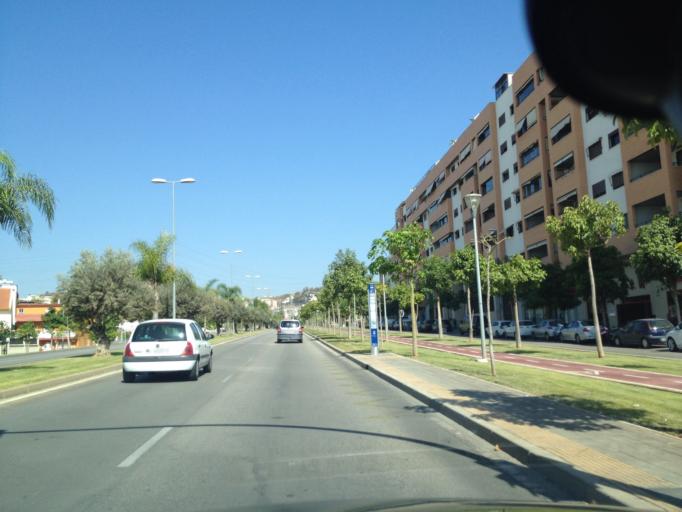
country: ES
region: Andalusia
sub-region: Provincia de Malaga
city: Malaga
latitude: 36.7216
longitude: -4.4693
